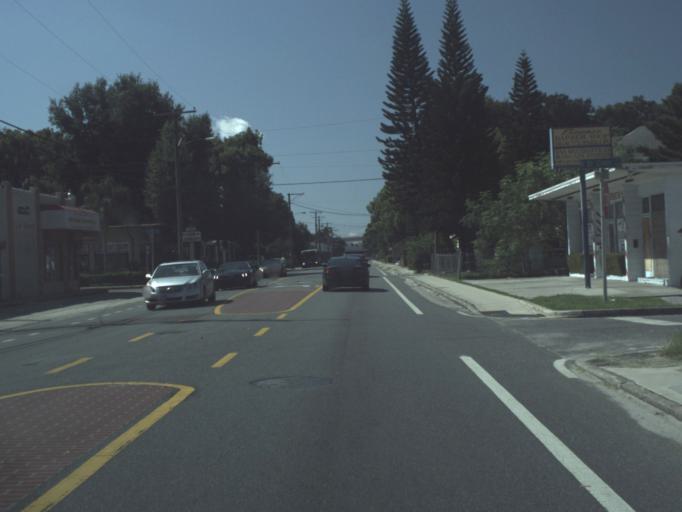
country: US
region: Florida
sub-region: Hillsborough County
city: Tampa
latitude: 27.9702
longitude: -82.4512
